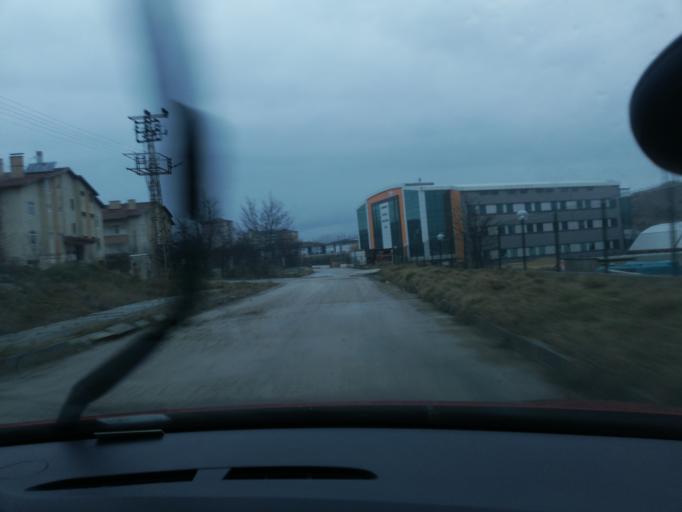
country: TR
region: Kastamonu
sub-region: Cide
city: Kastamonu
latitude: 41.4224
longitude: 33.8001
